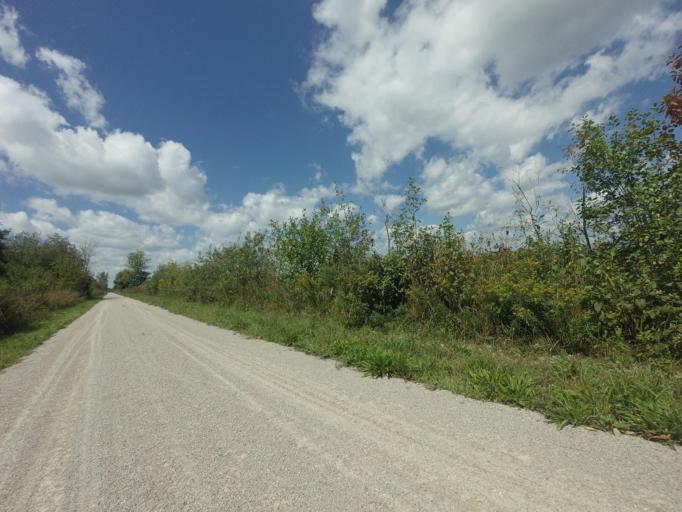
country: CA
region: Ontario
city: Huron East
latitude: 43.6044
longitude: -81.1159
